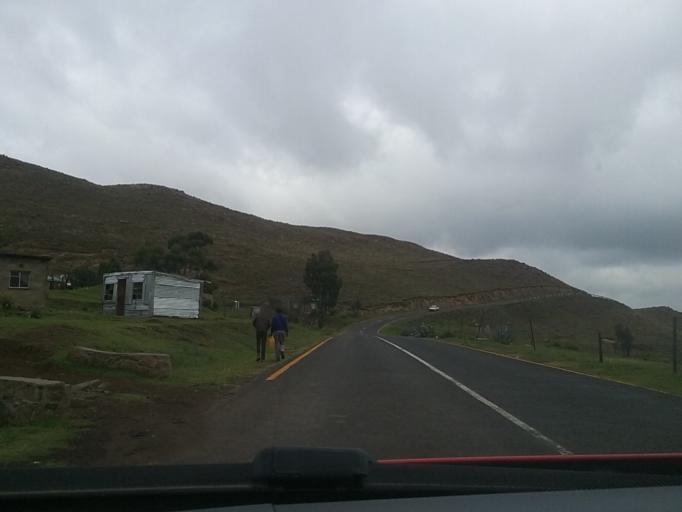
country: LS
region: Berea
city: Teyateyaneng
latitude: -29.2312
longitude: 27.8679
